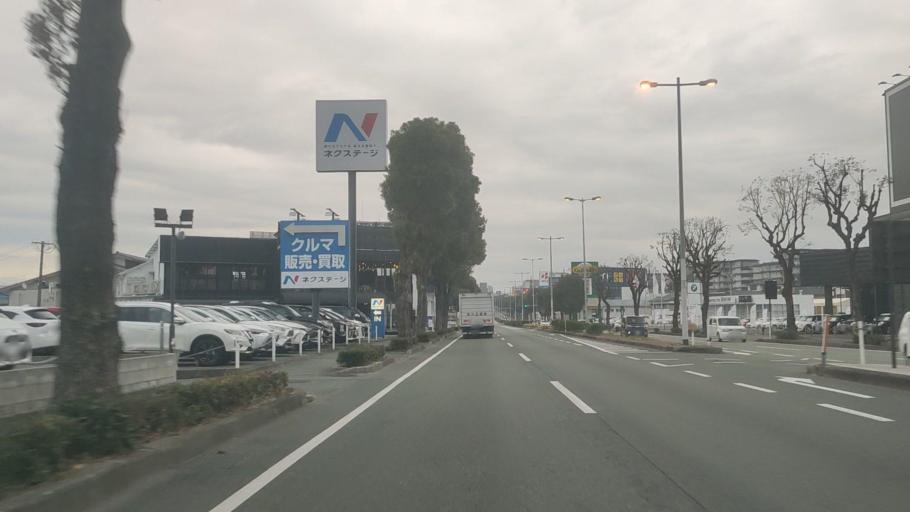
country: JP
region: Kumamoto
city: Kumamoto
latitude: 32.8177
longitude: 130.7533
